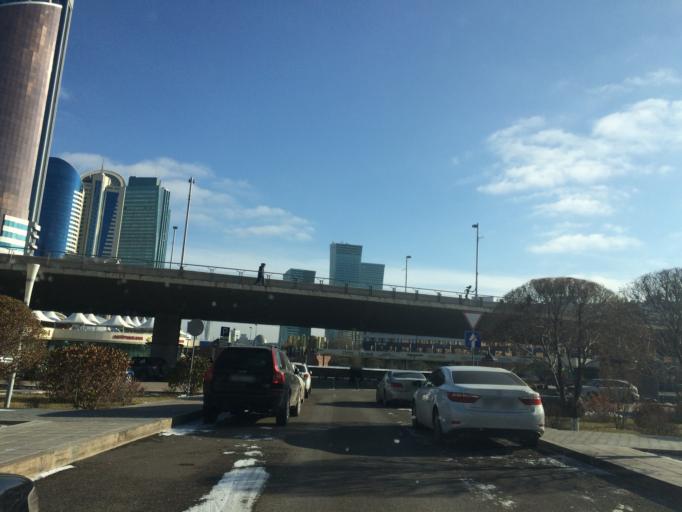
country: KZ
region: Astana Qalasy
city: Astana
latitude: 51.1313
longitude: 71.4132
